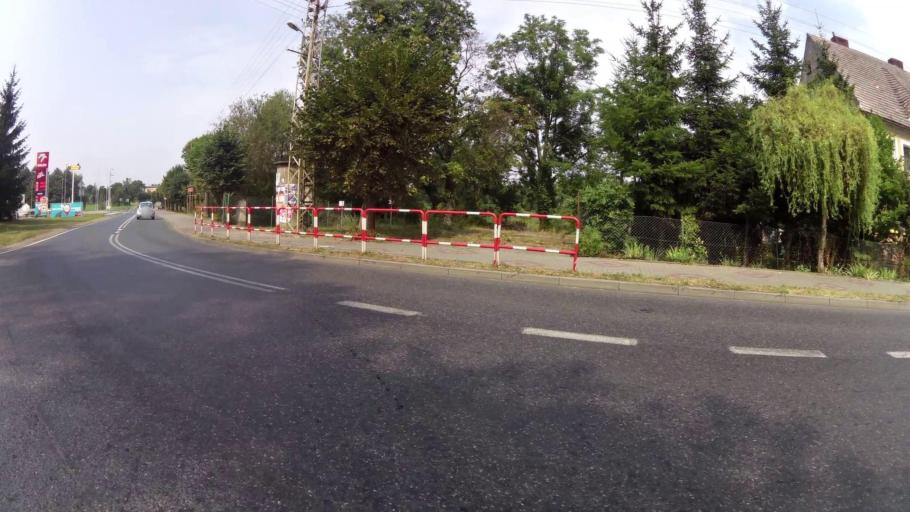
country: PL
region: West Pomeranian Voivodeship
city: Trzcinsko Zdroj
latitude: 52.9616
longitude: 14.6164
